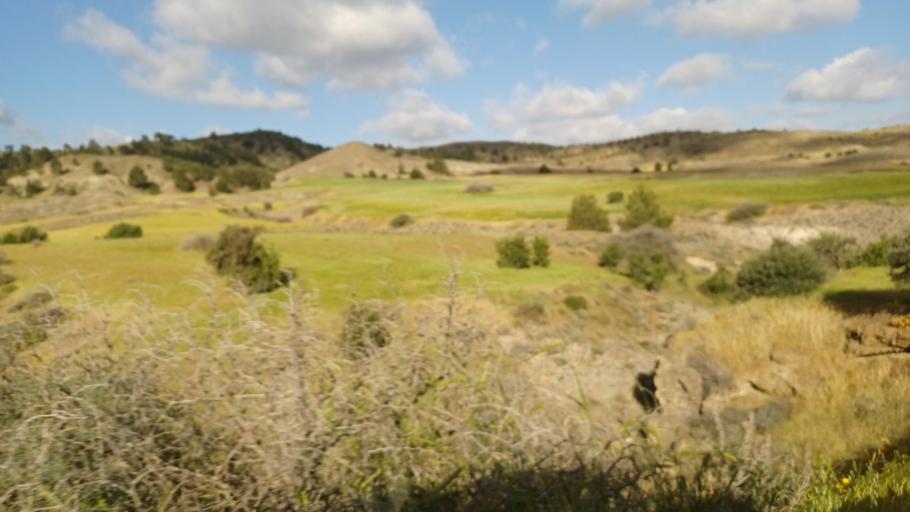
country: CY
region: Lefkosia
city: Peristerona
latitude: 35.0690
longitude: 33.0465
